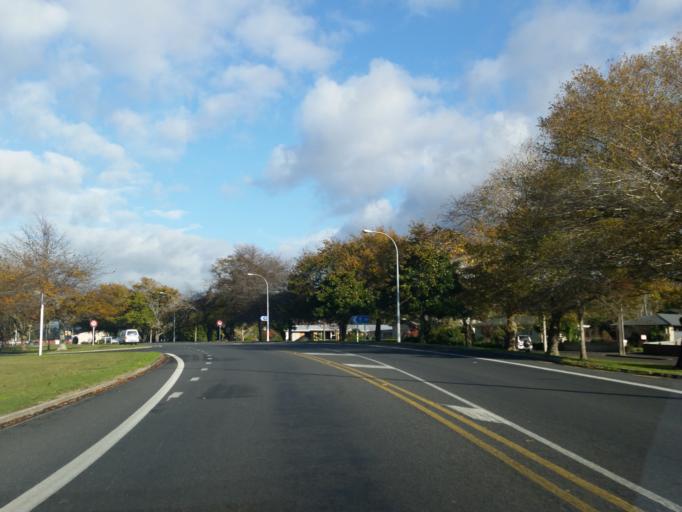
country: NZ
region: Waikato
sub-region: Hauraki District
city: Waihi
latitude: -37.3923
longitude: 175.8340
